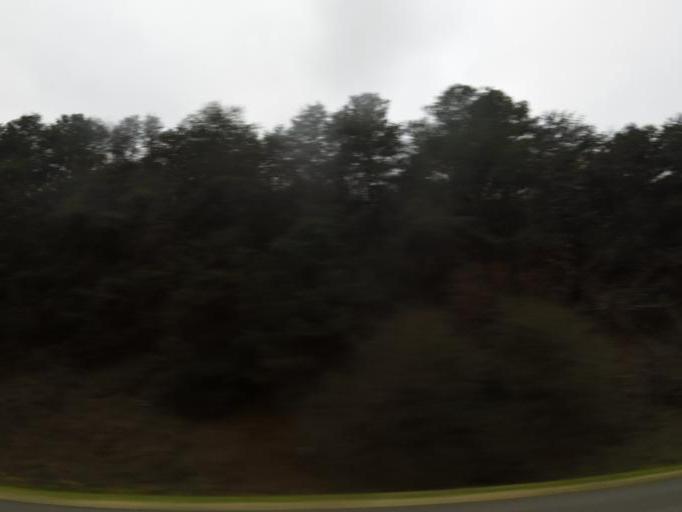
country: US
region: Alabama
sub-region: Jefferson County
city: Morris
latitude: 33.7379
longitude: -86.8259
